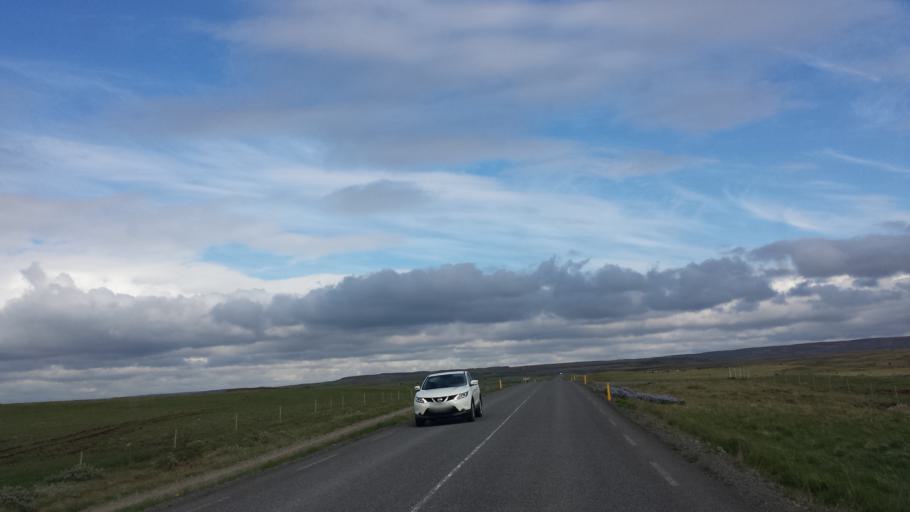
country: IS
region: South
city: Vestmannaeyjar
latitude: 64.3079
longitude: -20.2096
